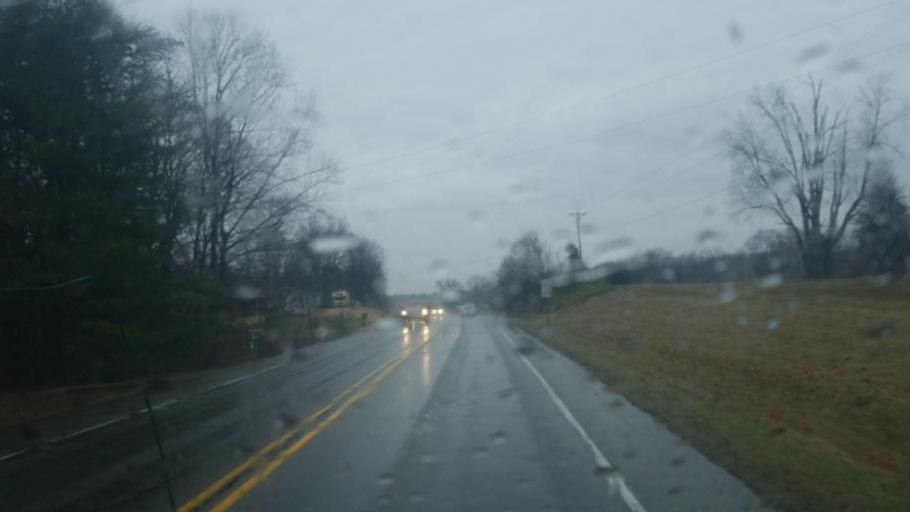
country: US
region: Indiana
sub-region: Bartholomew County
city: Columbus
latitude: 39.2053
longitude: -85.8673
